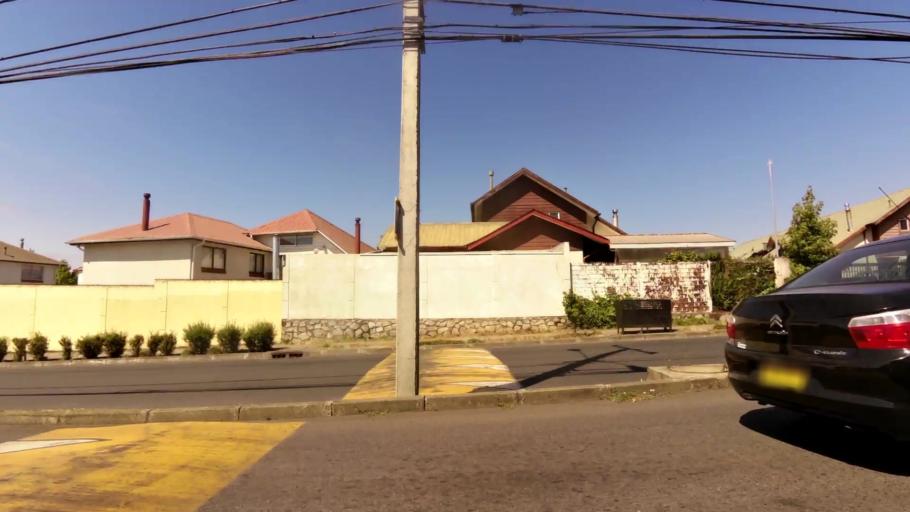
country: CL
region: Biobio
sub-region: Provincia de Concepcion
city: Concepcion
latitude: -36.7858
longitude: -73.0431
